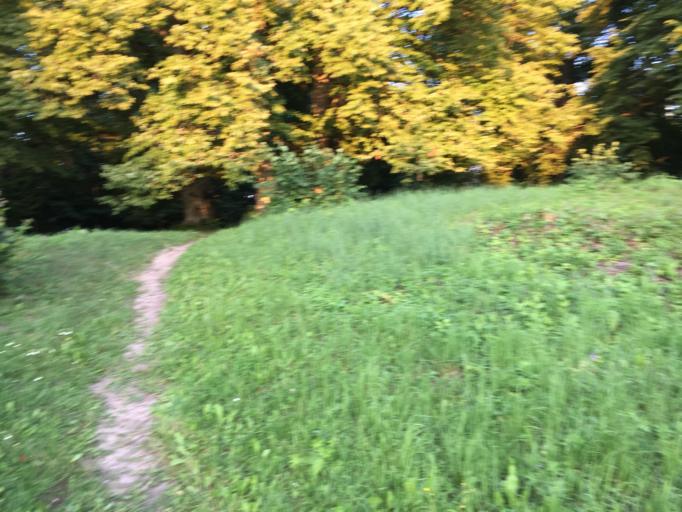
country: LV
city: Tervete
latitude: 56.4818
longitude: 23.3854
